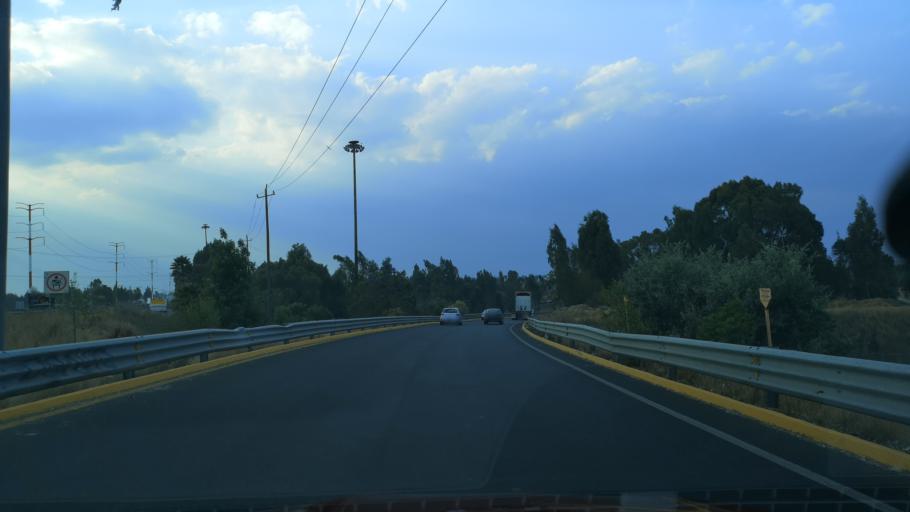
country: MX
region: Puebla
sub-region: Juan C. Bonilla
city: Santa Maria Zacatepec
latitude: 19.1319
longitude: -98.3729
